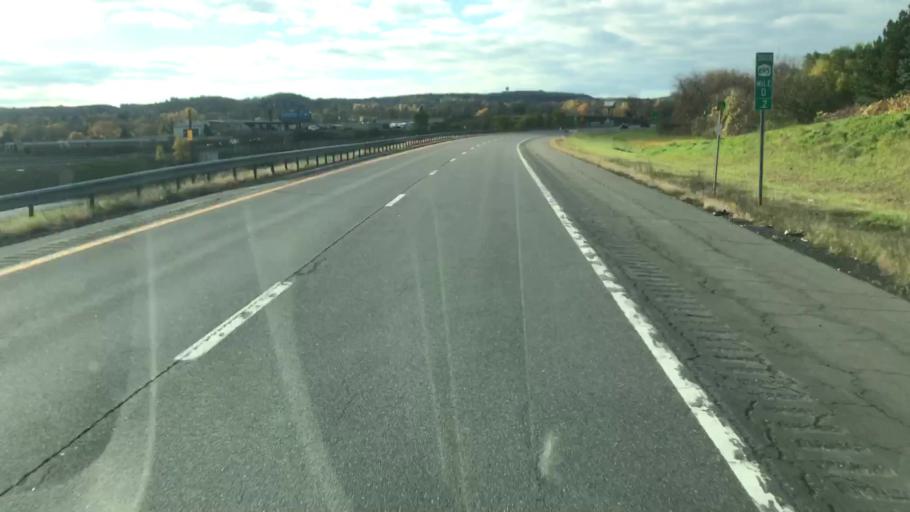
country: US
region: New York
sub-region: Onondaga County
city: Fairmount
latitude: 43.0578
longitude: -76.2376
